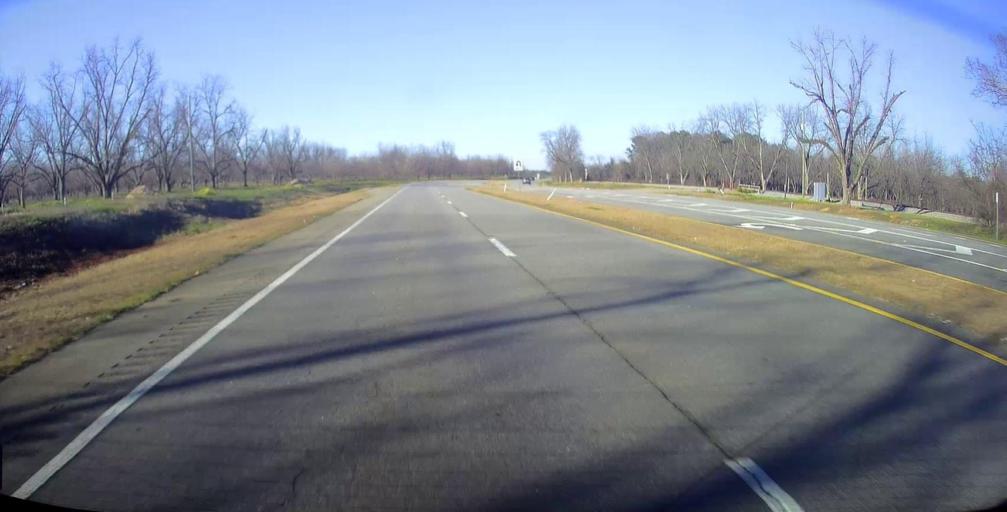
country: US
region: Georgia
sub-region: Sumter County
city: Americus
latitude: 31.9565
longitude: -84.2559
